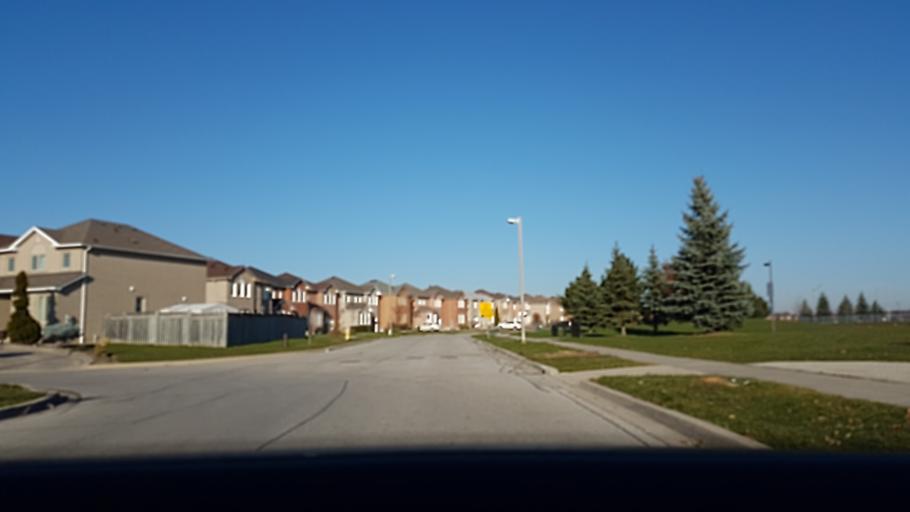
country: CA
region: Ontario
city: Vaughan
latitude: 43.7918
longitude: -79.5589
